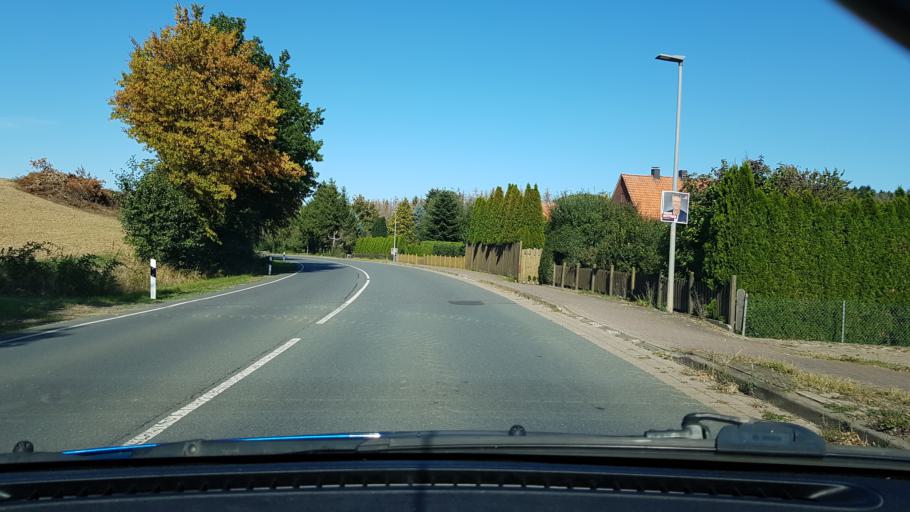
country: DE
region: Lower Saxony
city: Bad Munder am Deister
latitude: 52.2267
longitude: 9.4355
